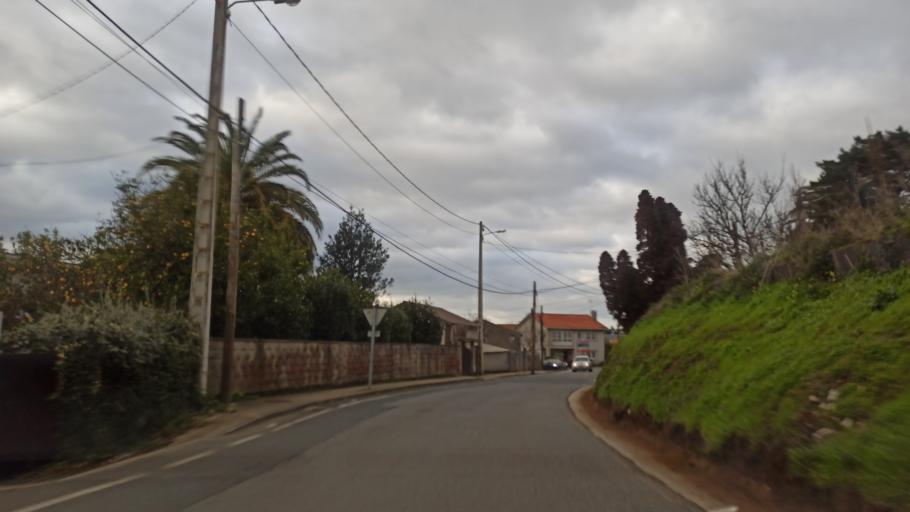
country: ES
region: Galicia
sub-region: Provincia da Coruna
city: Oleiros
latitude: 43.3318
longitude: -8.3548
